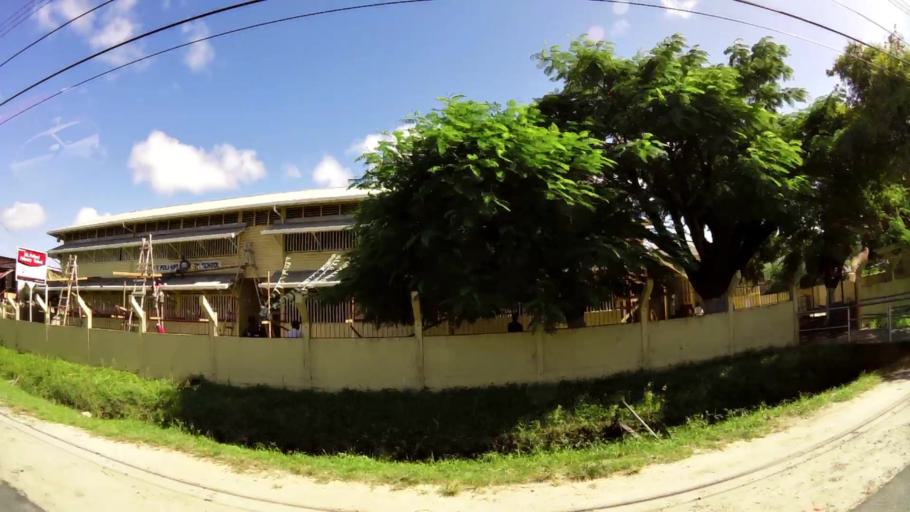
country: GY
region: Demerara-Mahaica
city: Georgetown
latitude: 6.8223
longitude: -58.1407
